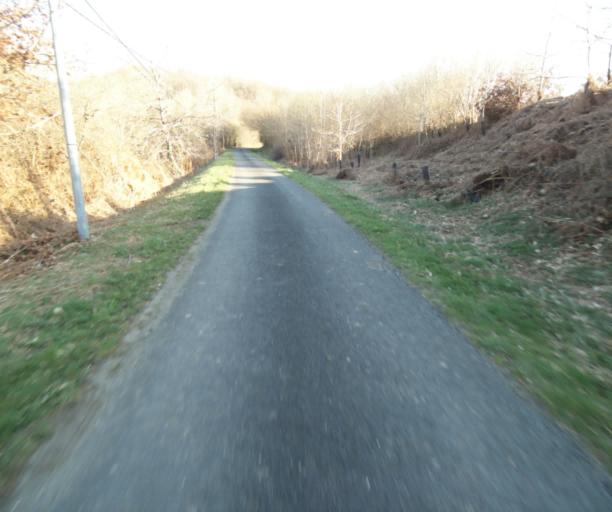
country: FR
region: Limousin
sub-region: Departement de la Correze
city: Saint-Clement
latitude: 45.3473
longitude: 1.6709
